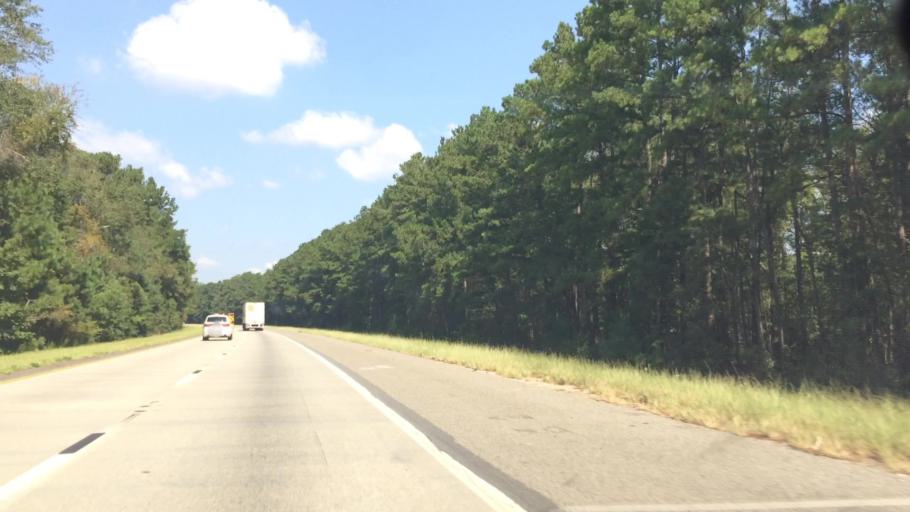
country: US
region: South Carolina
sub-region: Colleton County
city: Walterboro
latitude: 33.0188
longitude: -80.6655
